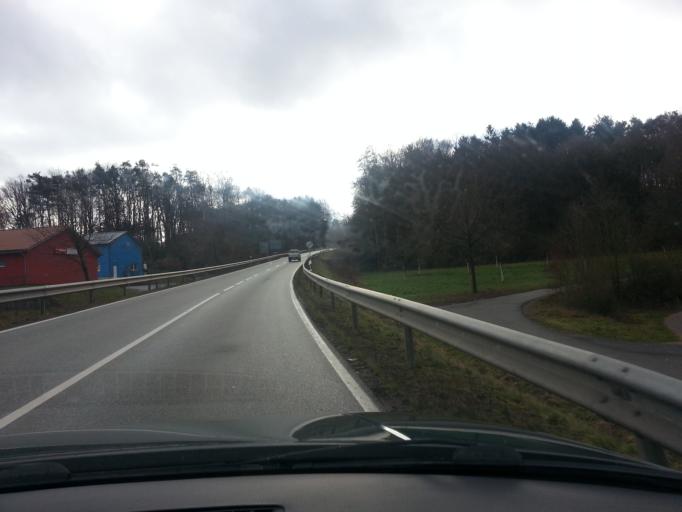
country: DE
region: Rheinland-Pfalz
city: Schwedelbach
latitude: 49.4927
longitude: 7.5858
